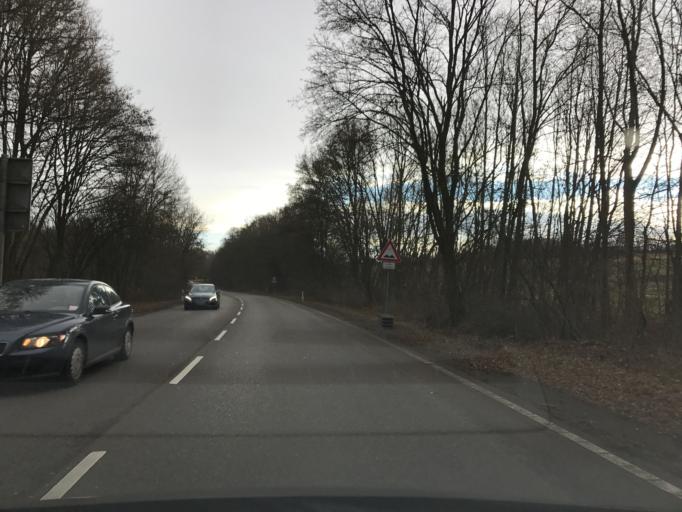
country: DE
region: Baden-Wuerttemberg
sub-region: Regierungsbezirk Stuttgart
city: Stuttgart-Ost
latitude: 48.7442
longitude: 9.2001
